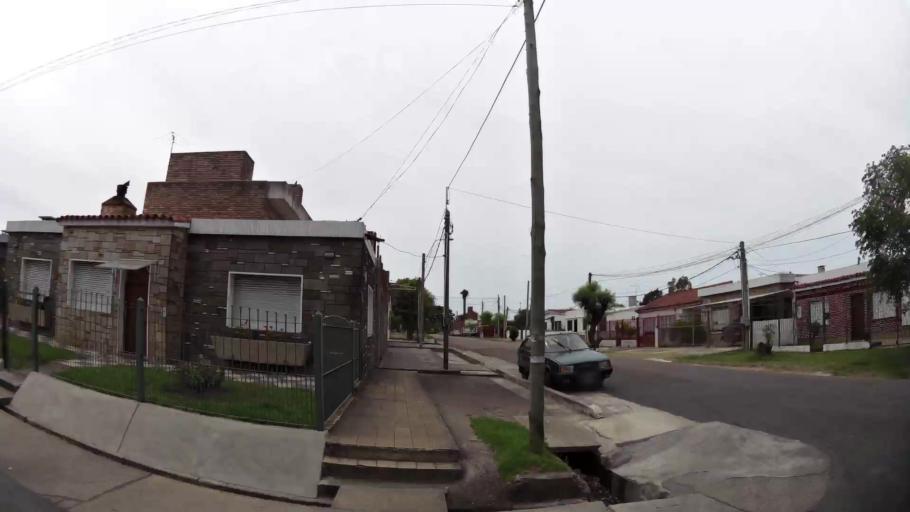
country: UY
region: Canelones
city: Las Piedras
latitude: -34.7300
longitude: -56.2276
